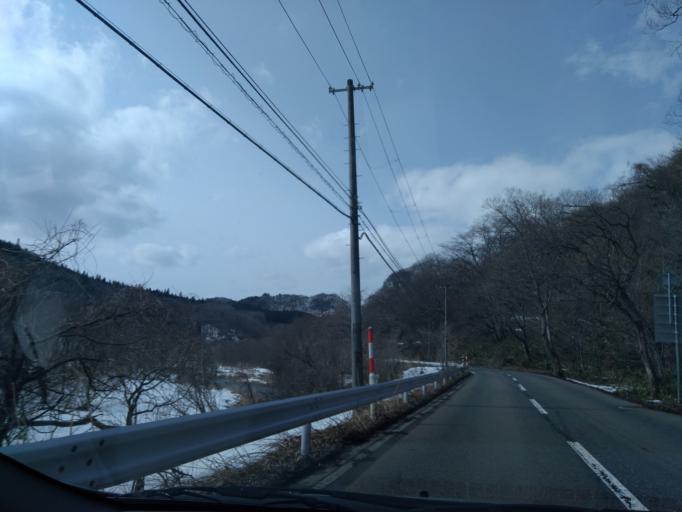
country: JP
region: Iwate
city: Kitakami
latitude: 39.2383
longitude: 140.9649
